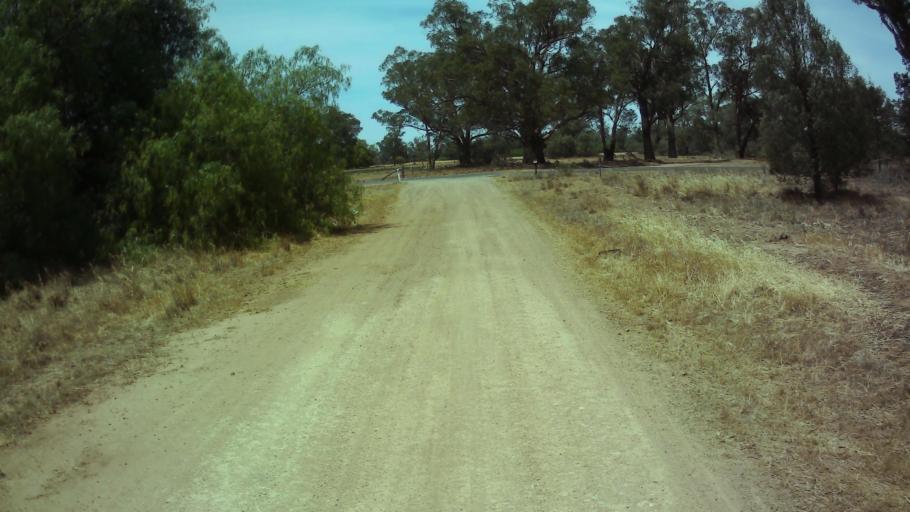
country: AU
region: New South Wales
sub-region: Weddin
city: Grenfell
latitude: -34.0370
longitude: 147.9235
